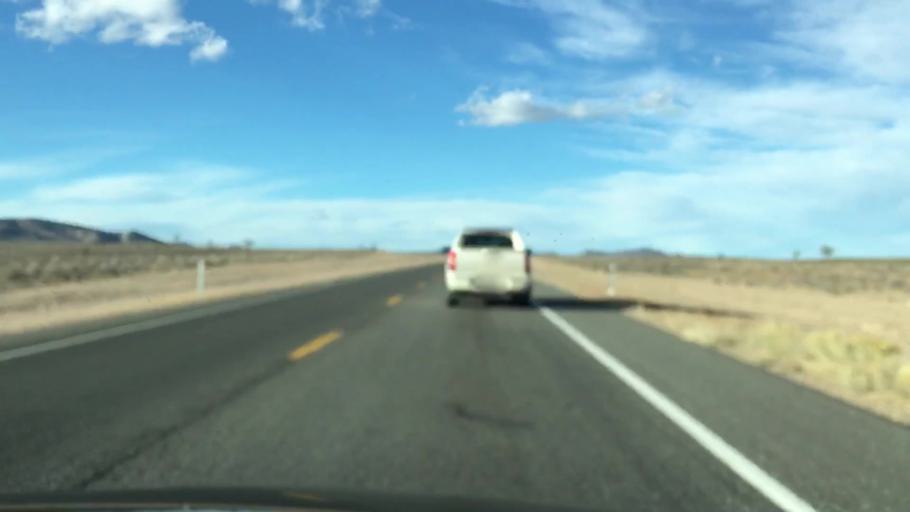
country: US
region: Nevada
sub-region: Esmeralda County
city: Goldfield
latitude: 37.5751
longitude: -117.2030
